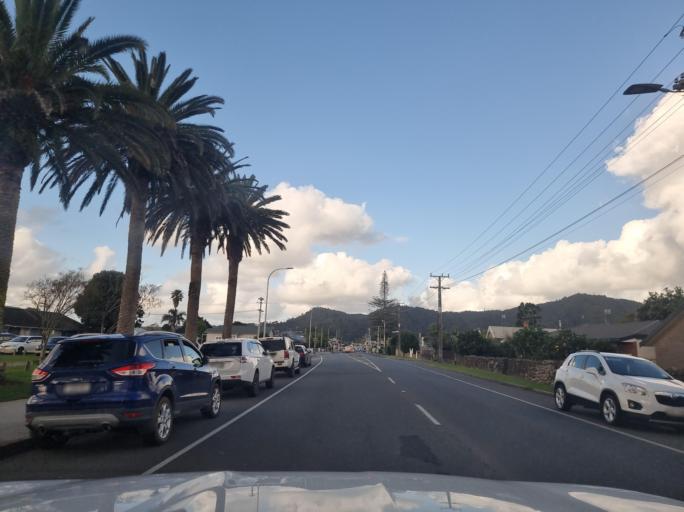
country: NZ
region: Northland
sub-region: Whangarei
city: Whangarei
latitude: -35.7095
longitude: 174.3168
